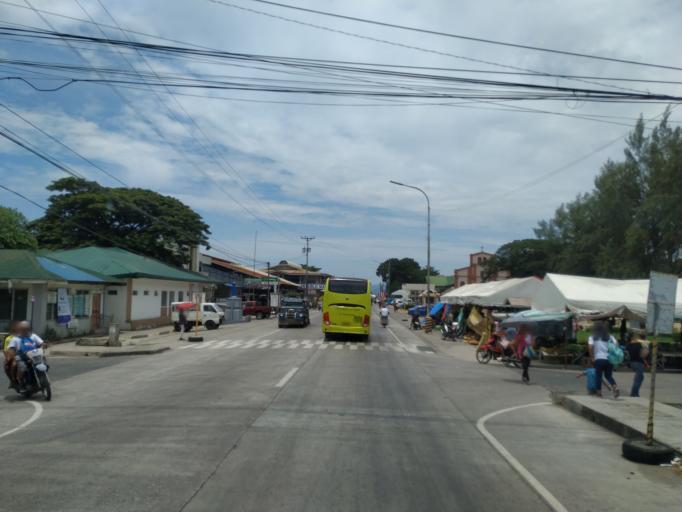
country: PH
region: Central Visayas
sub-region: Province of Negros Oriental
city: Sibulan
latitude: 9.3582
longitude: 123.2850
